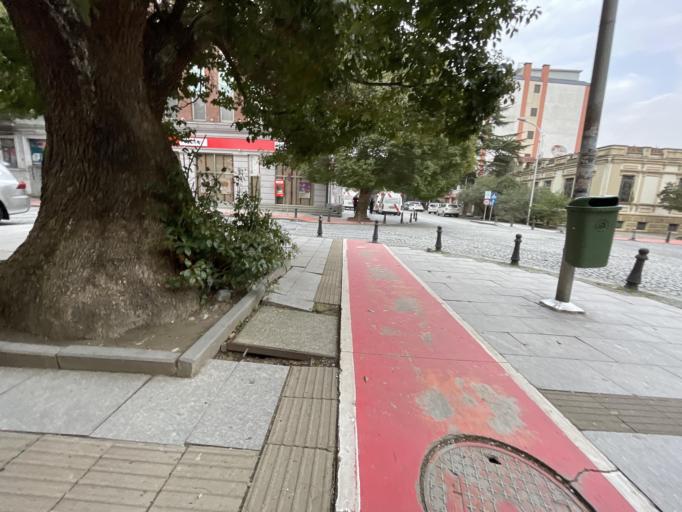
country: GE
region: Ajaria
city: Batumi
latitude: 41.6474
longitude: 41.6356
